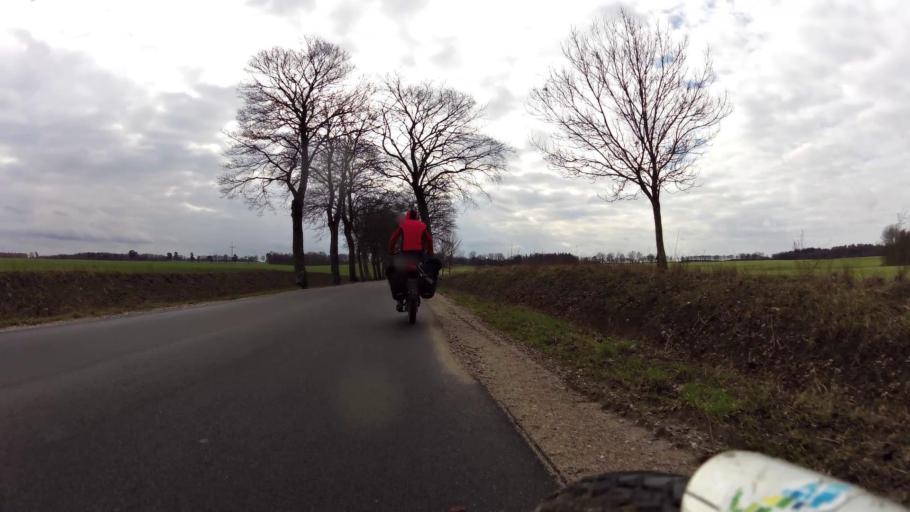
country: PL
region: Pomeranian Voivodeship
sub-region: Powiat bytowski
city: Kolczyglowy
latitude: 54.2302
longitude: 17.2420
